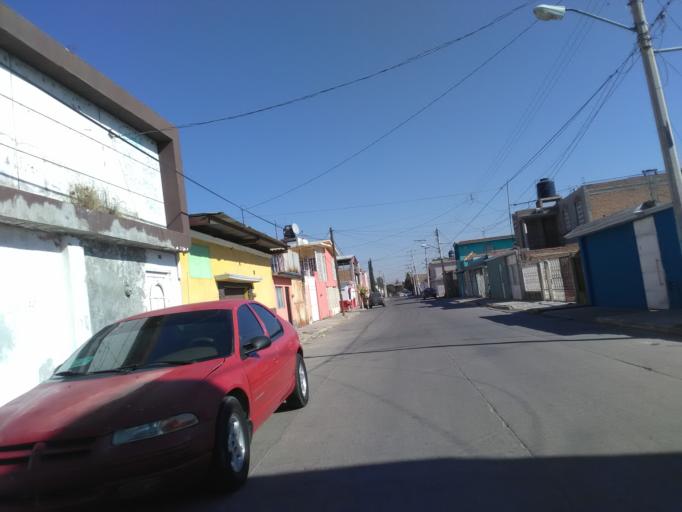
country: MX
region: Durango
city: Victoria de Durango
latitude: 24.0135
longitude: -104.6432
